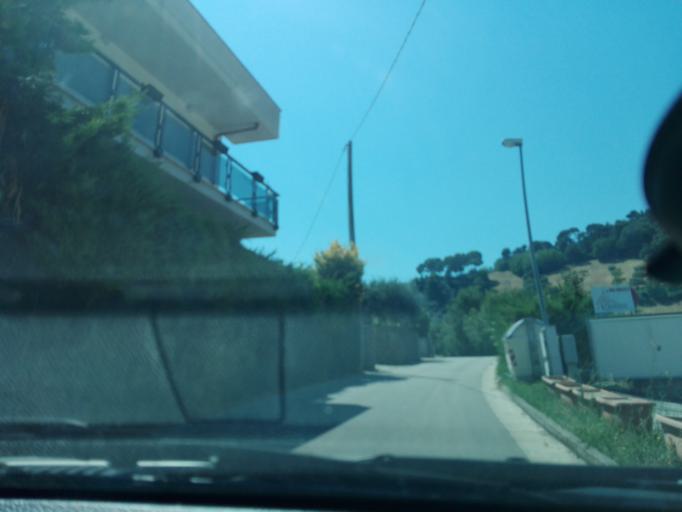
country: IT
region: Abruzzo
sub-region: Provincia di Pescara
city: Montesilvano Marina
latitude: 42.5018
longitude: 14.1567
